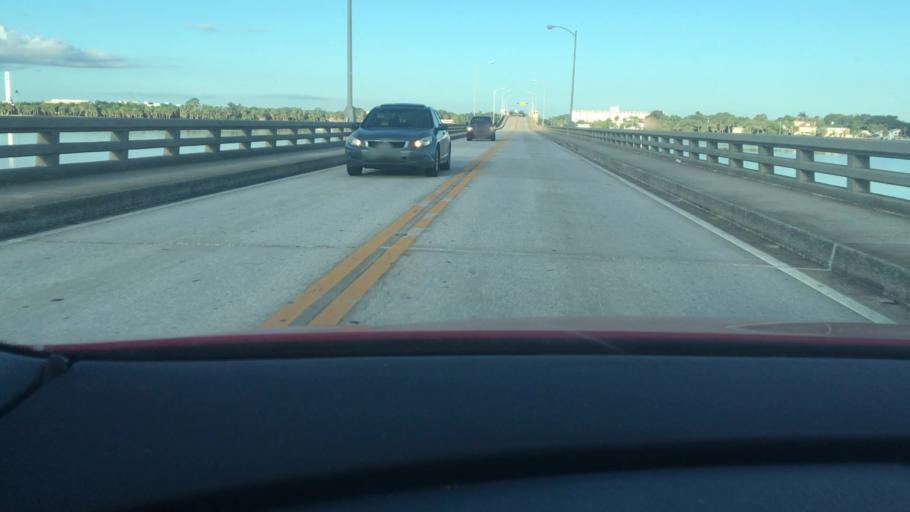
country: US
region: Florida
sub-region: Volusia County
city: Daytona Beach
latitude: 29.2243
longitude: -81.0164
